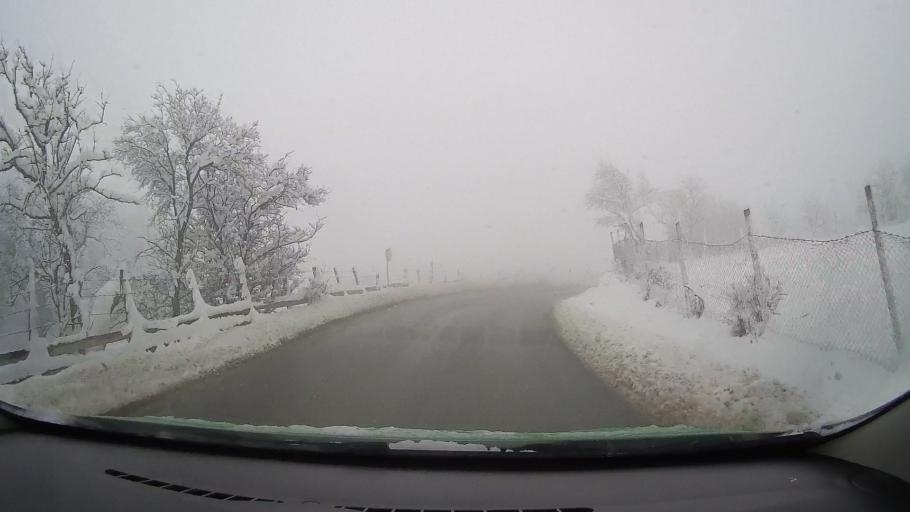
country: RO
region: Sibiu
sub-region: Comuna Jina
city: Jina
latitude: 45.7861
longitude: 23.6875
